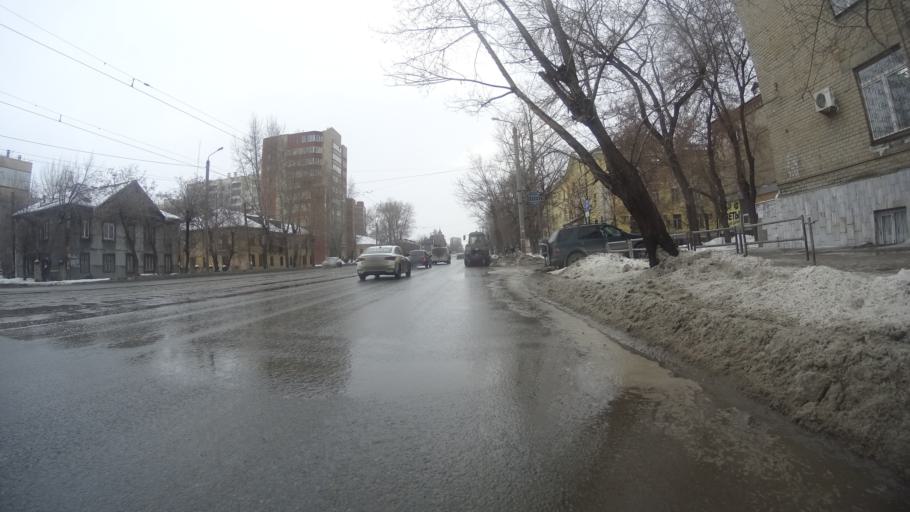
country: RU
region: Chelyabinsk
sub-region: Gorod Chelyabinsk
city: Chelyabinsk
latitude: 55.1420
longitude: 61.3827
